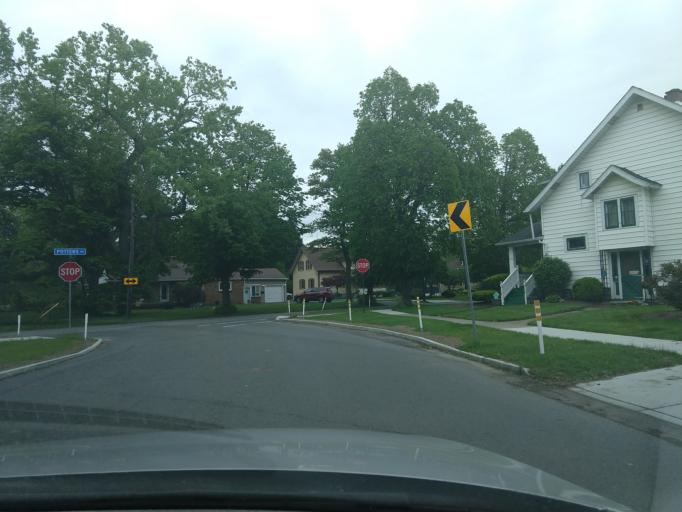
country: US
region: New York
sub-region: Erie County
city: West Seneca
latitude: 42.8423
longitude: -78.8057
